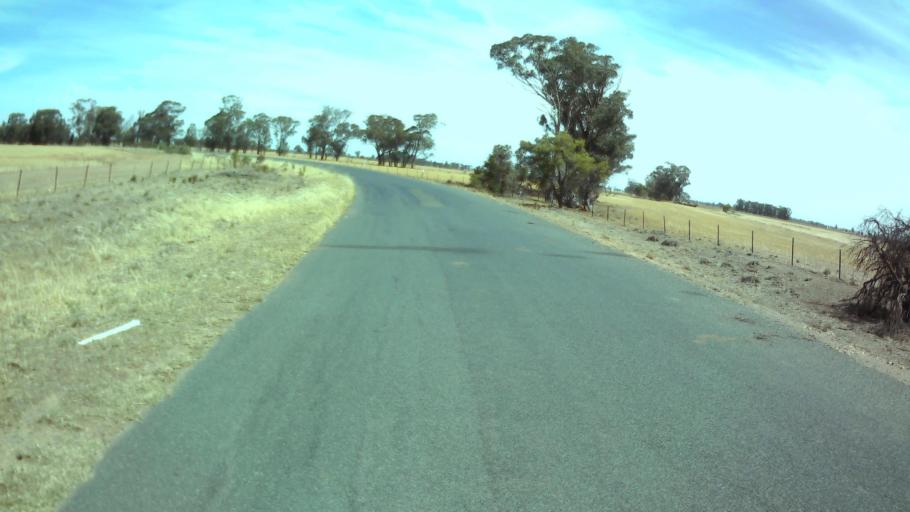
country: AU
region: New South Wales
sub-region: Weddin
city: Grenfell
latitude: -33.9545
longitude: 147.7771
